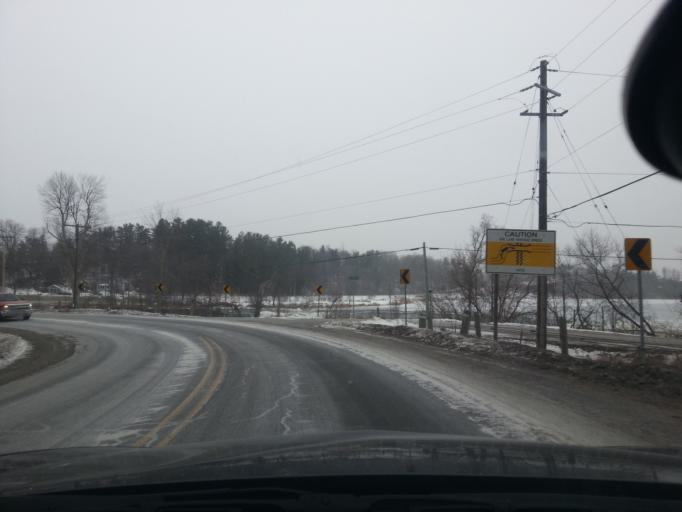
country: CA
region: Ontario
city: Arnprior
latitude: 45.3357
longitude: -76.2852
